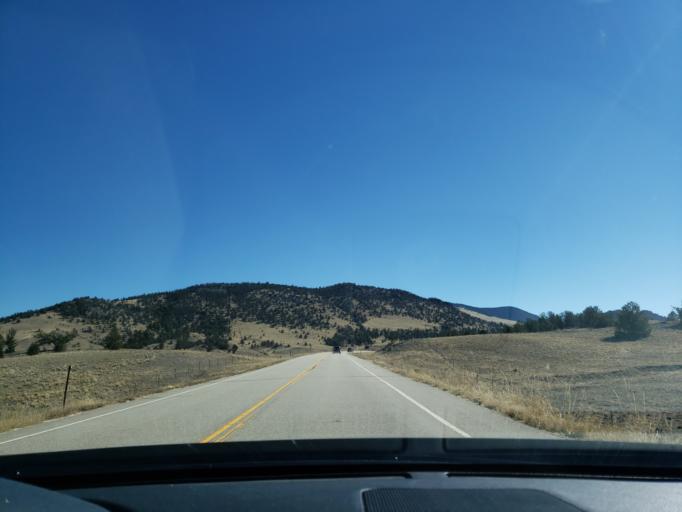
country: US
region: Colorado
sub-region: Chaffee County
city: Buena Vista
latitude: 38.8630
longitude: -105.6618
